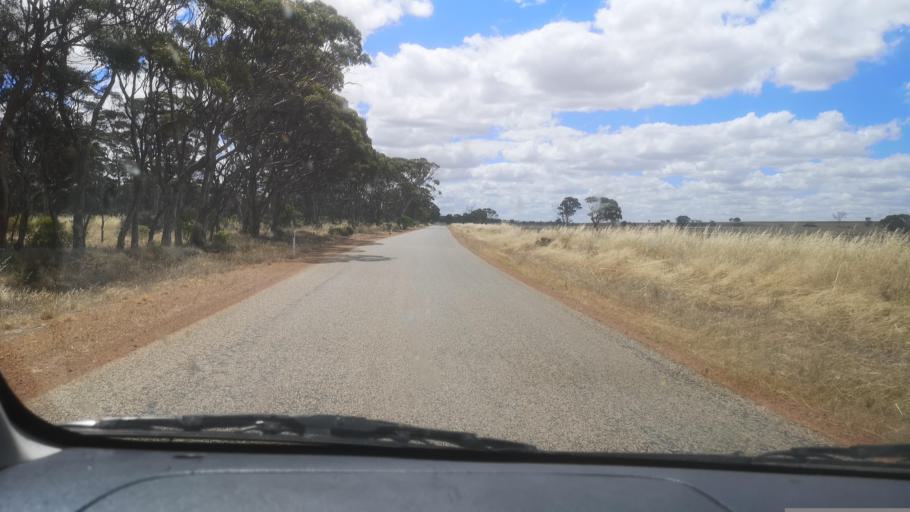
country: AU
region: Western Australia
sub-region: Cunderdin
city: Cunderdin
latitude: -32.0494
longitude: 117.4132
